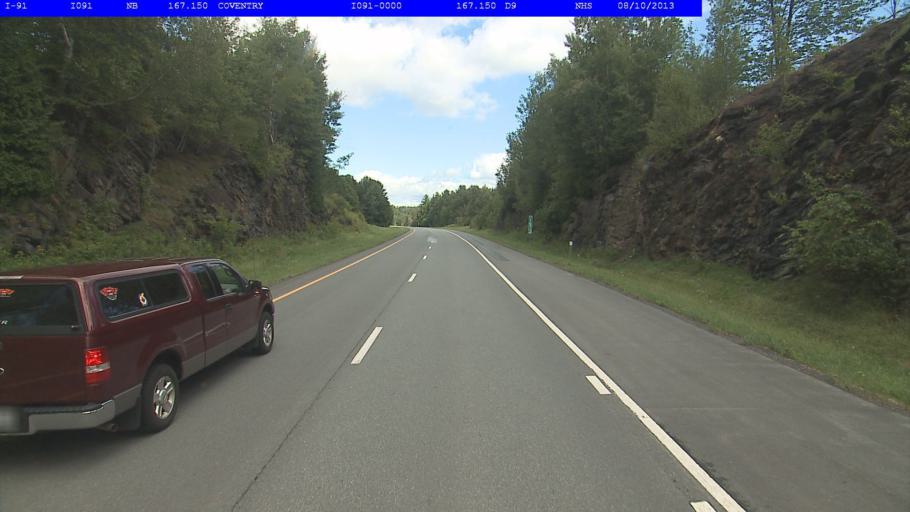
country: US
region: Vermont
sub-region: Orleans County
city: Newport
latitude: 44.8813
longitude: -72.1713
